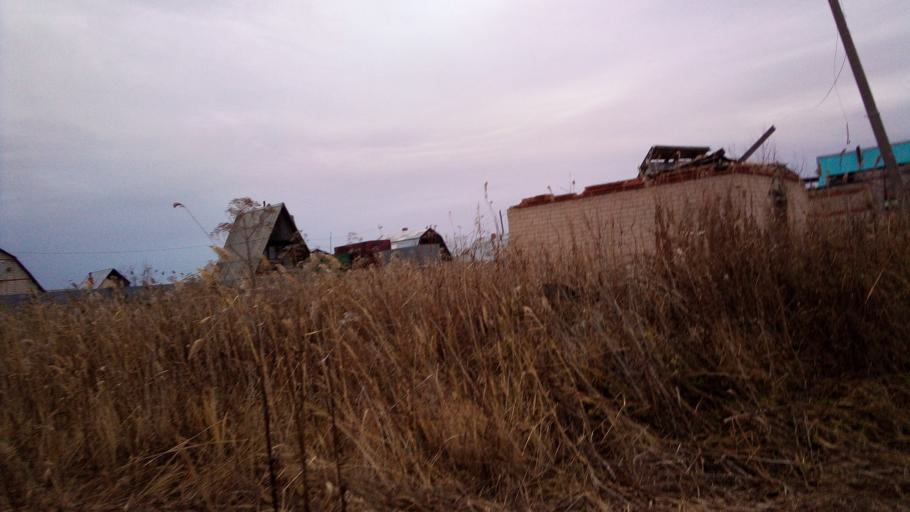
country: RU
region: Chelyabinsk
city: Novosineglazovskiy
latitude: 54.9852
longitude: 61.4032
